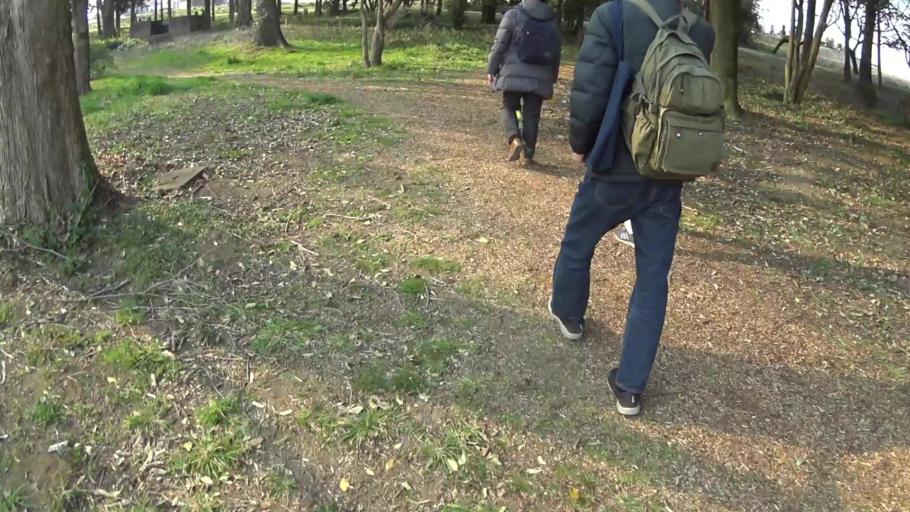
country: JP
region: Ibaraki
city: Koga
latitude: 36.1799
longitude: 139.7006
